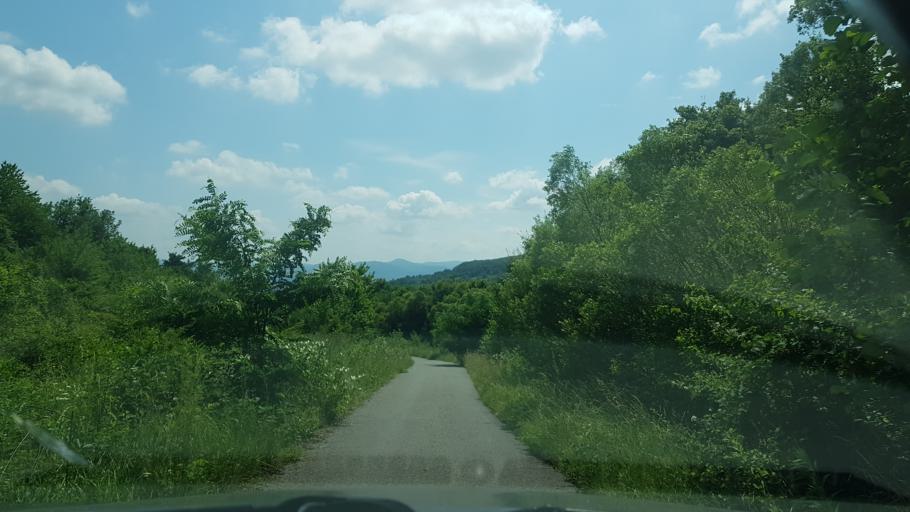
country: HU
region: Borsod-Abauj-Zemplen
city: Gonc
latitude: 48.5506
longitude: 21.4898
